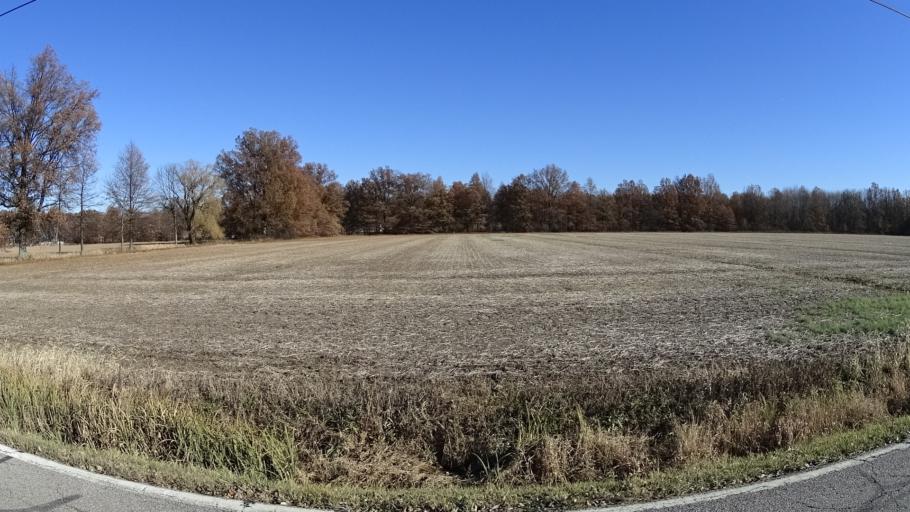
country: US
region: Ohio
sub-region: Lorain County
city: Avon Center
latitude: 41.4393
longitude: -81.9787
